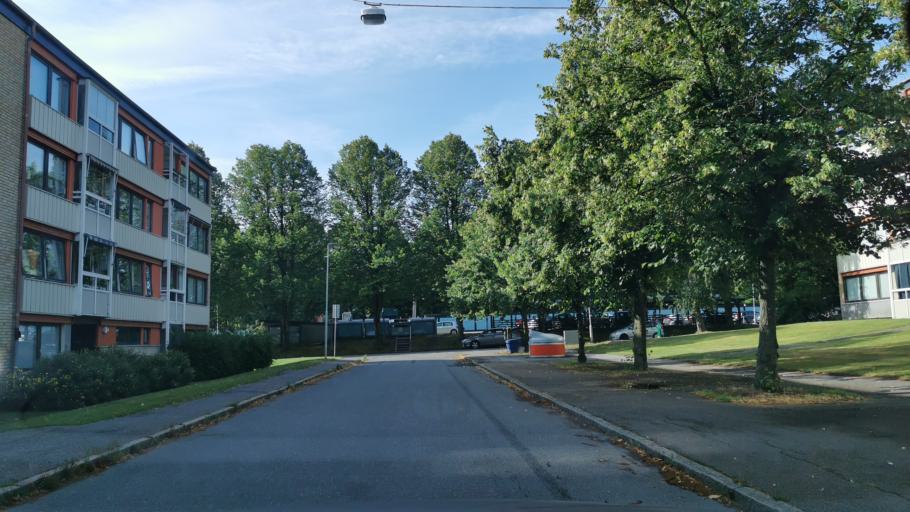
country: SE
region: Vaestra Goetaland
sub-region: Goteborg
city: Majorna
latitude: 57.6611
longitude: 11.9280
